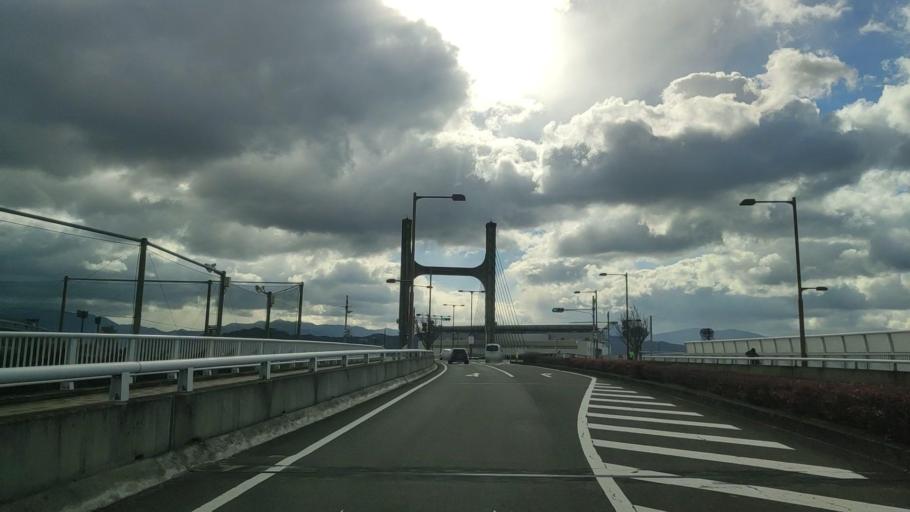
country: JP
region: Ehime
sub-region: Shikoku-chuo Shi
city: Matsuyama
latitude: 33.8118
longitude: 132.7412
